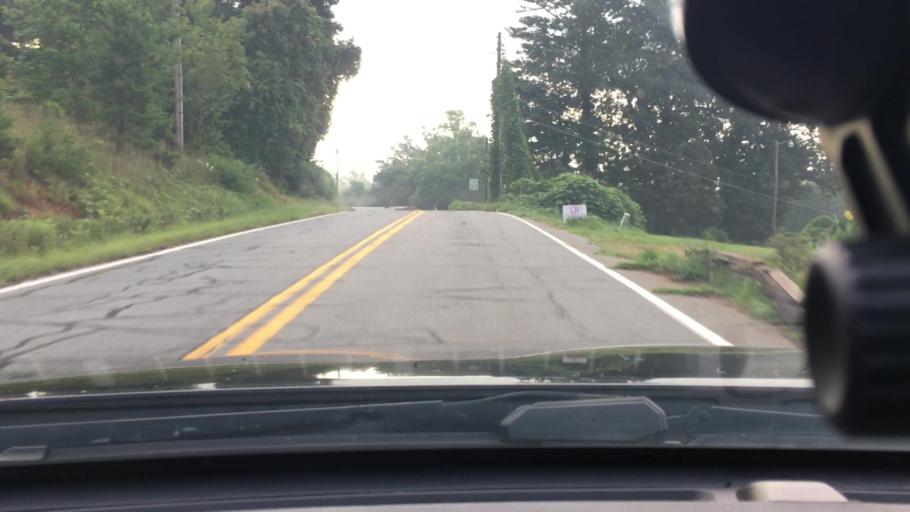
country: US
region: North Carolina
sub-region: Rutherford County
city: Rutherfordton
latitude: 35.3760
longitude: -81.9688
